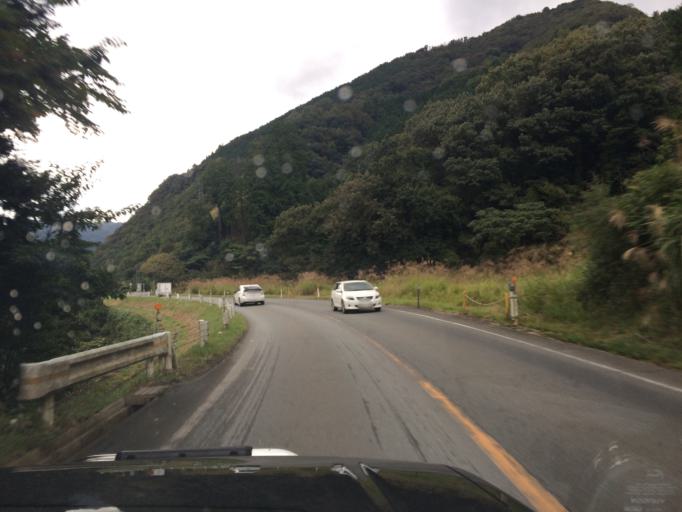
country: JP
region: Hyogo
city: Toyooka
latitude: 35.4418
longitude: 134.7922
